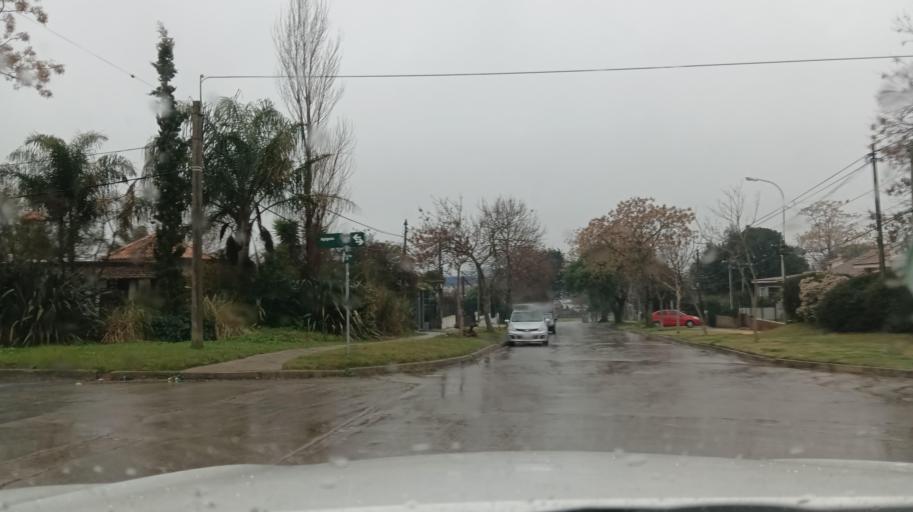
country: UY
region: Canelones
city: Paso de Carrasco
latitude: -34.8749
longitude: -56.0869
